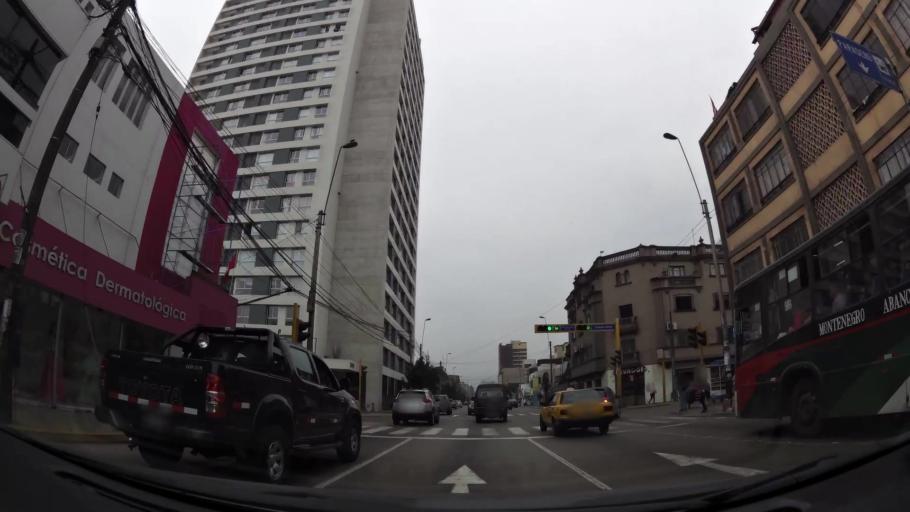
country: PE
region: Lima
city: Lima
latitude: -12.0797
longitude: -77.0340
